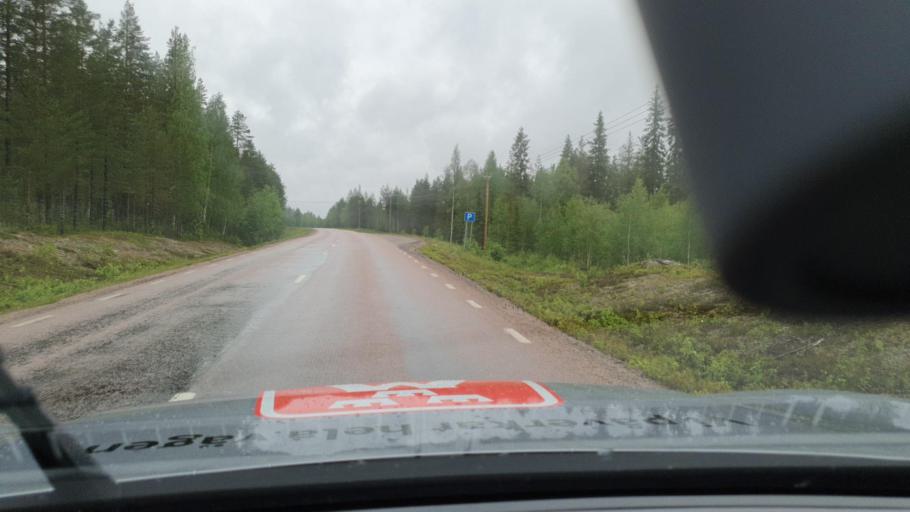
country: SE
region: Norrbotten
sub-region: Overkalix Kommun
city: OEverkalix
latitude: 66.4232
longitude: 22.9642
